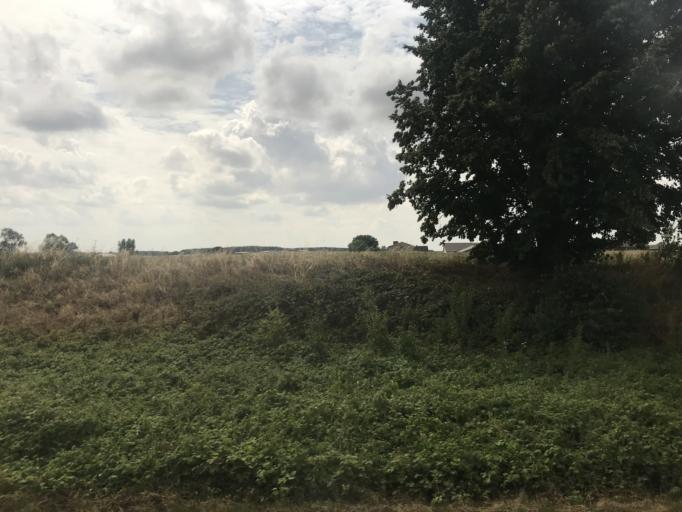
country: PL
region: Greater Poland Voivodeship
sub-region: Powiat gnieznienski
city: Lubowo
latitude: 52.5077
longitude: 17.4983
